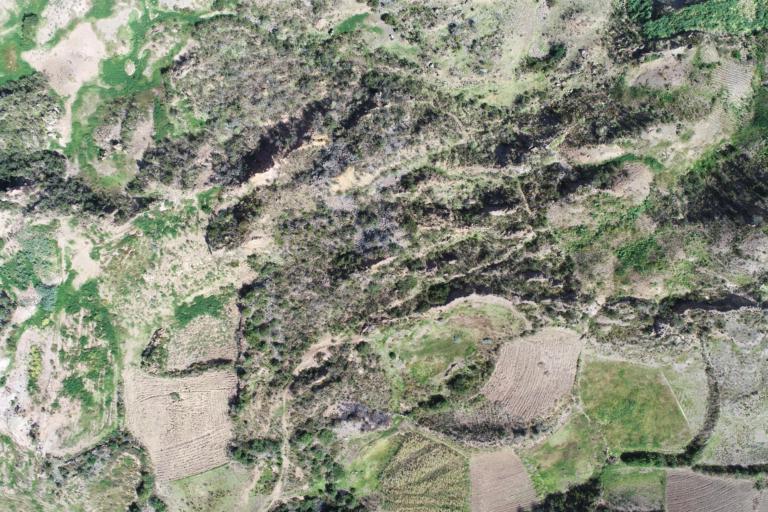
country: BO
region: La Paz
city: La Paz
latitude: -16.5584
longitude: -67.9882
